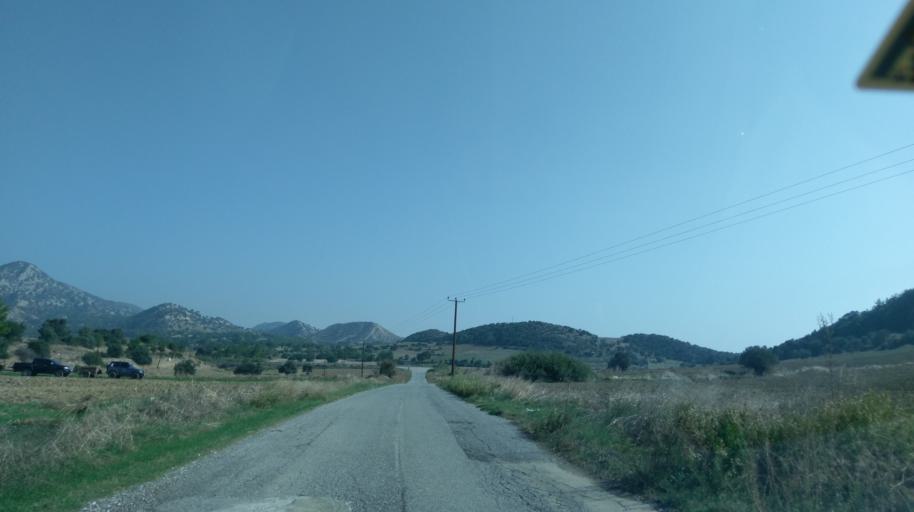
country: CY
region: Ammochostos
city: Lefkonoiko
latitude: 35.3314
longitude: 33.7165
